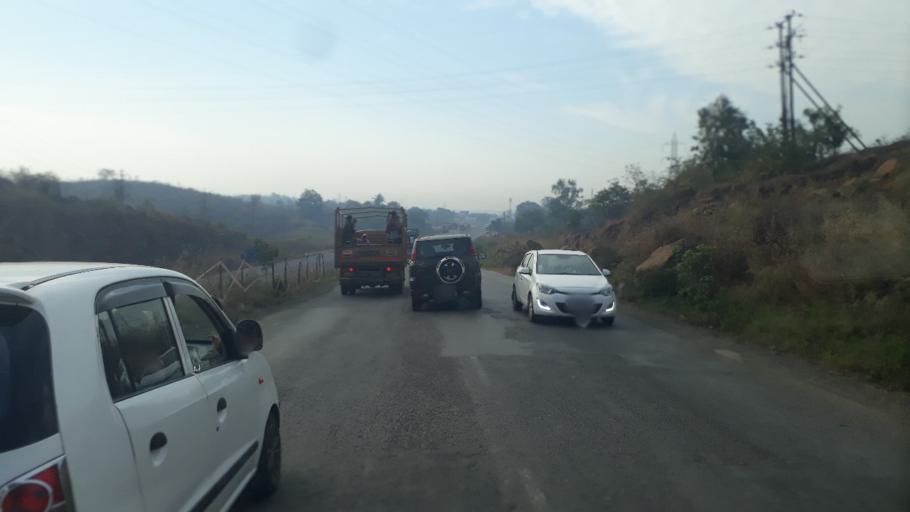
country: IN
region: Maharashtra
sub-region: Raigarh
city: Pen
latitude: 18.8256
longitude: 73.0933
